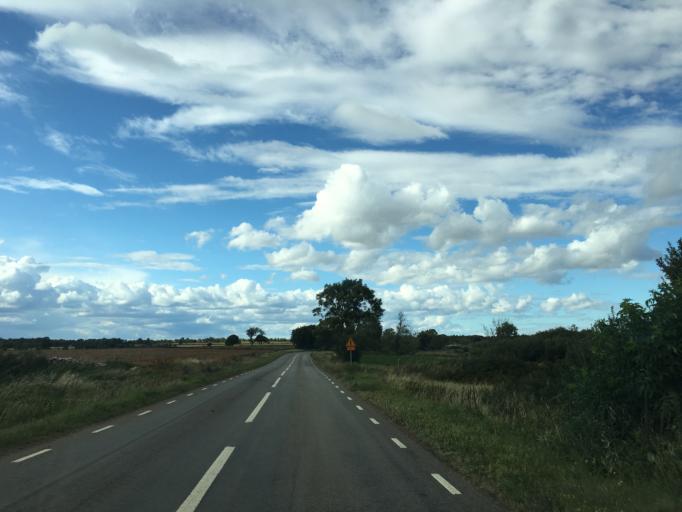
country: SE
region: Kalmar
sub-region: Morbylanga Kommun
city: Moerbylanga
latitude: 56.4244
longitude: 16.4354
